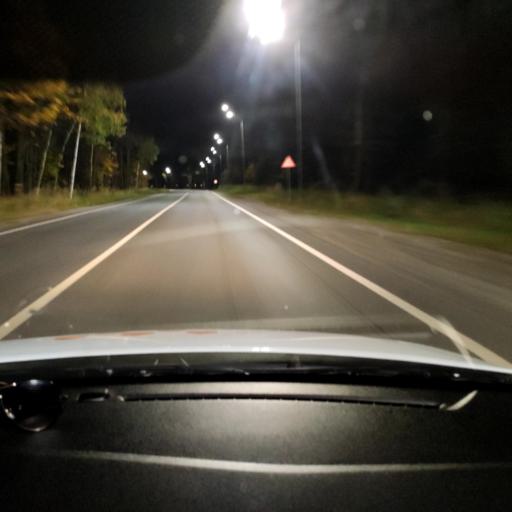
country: RU
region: Tatarstan
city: Stolbishchi
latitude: 55.6335
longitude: 49.0955
